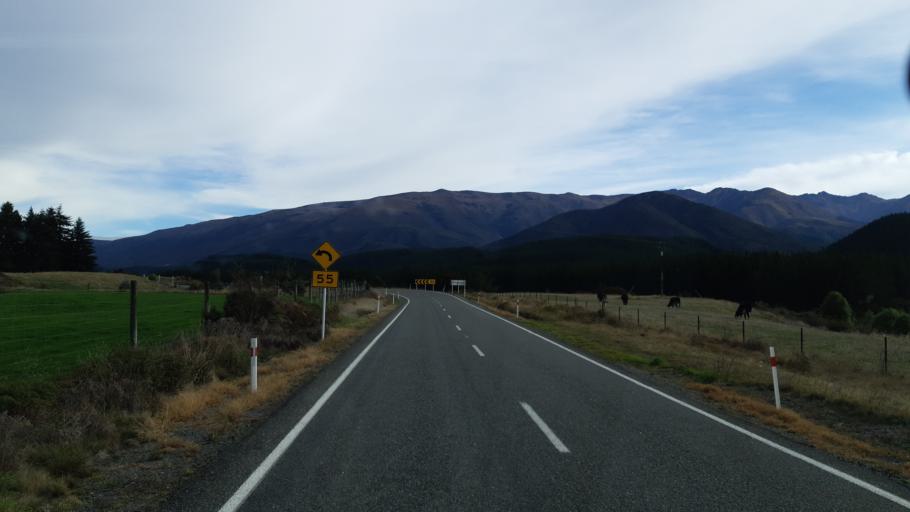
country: NZ
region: Tasman
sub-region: Tasman District
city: Brightwater
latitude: -41.6853
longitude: 173.1621
